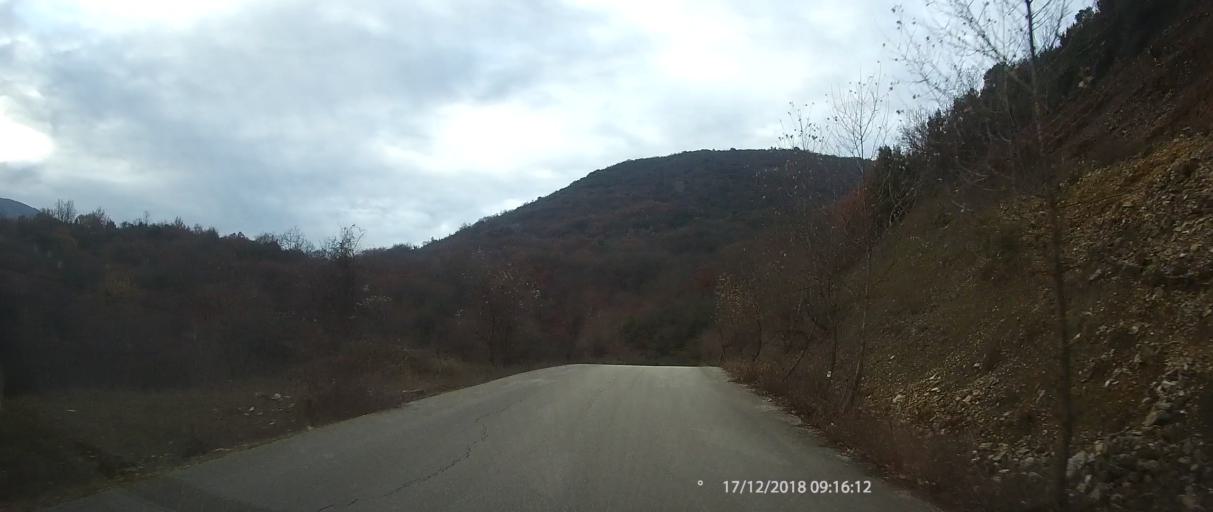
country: GR
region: Epirus
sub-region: Nomos Ioanninon
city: Kalpaki
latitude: 39.9623
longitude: 20.6568
